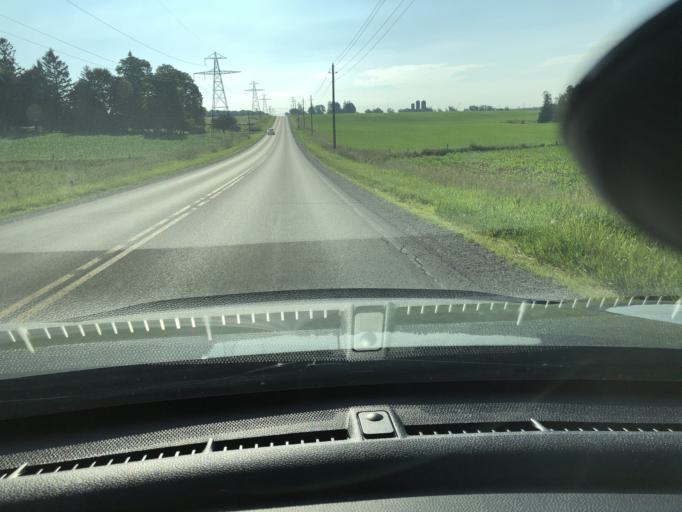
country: CA
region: Ontario
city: Stratford
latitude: 43.3887
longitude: -80.9184
